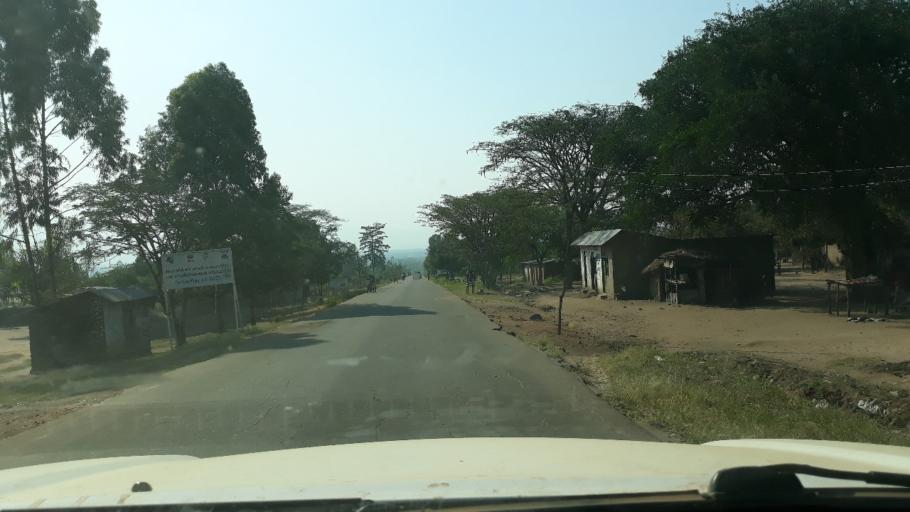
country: BI
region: Cibitoke
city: Cibitoke
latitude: -2.8972
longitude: 29.0497
